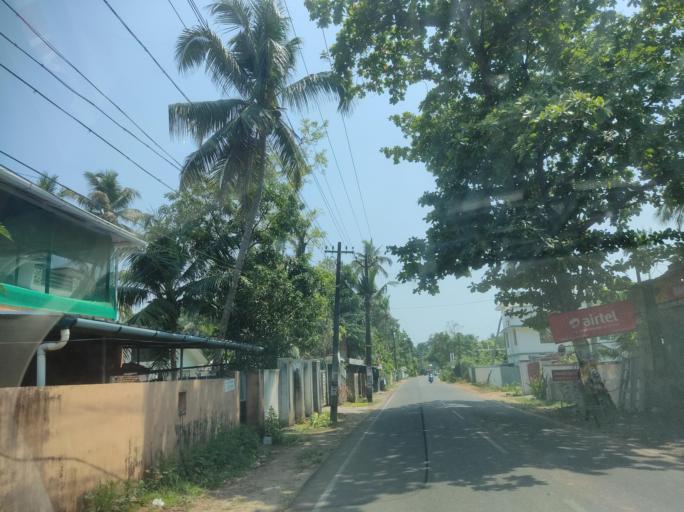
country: IN
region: Kerala
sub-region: Alappuzha
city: Kutiatodu
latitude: 9.8126
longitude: 76.3003
